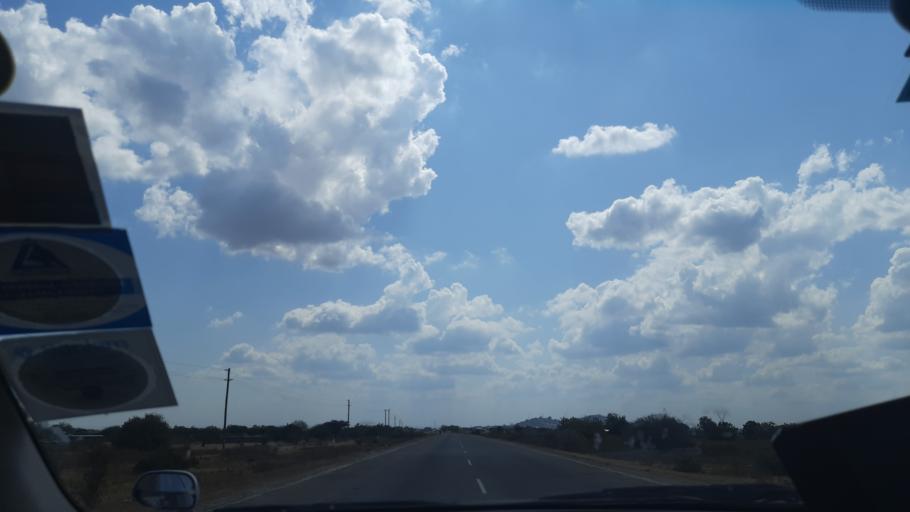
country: TZ
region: Singida
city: Kintinku
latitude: -5.9694
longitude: 35.3348
